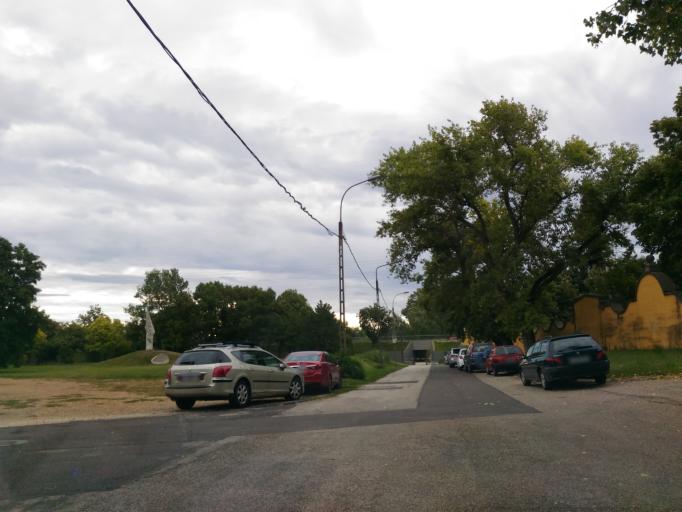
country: HU
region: Pest
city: Halasztelek
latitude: 47.3913
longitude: 18.9881
